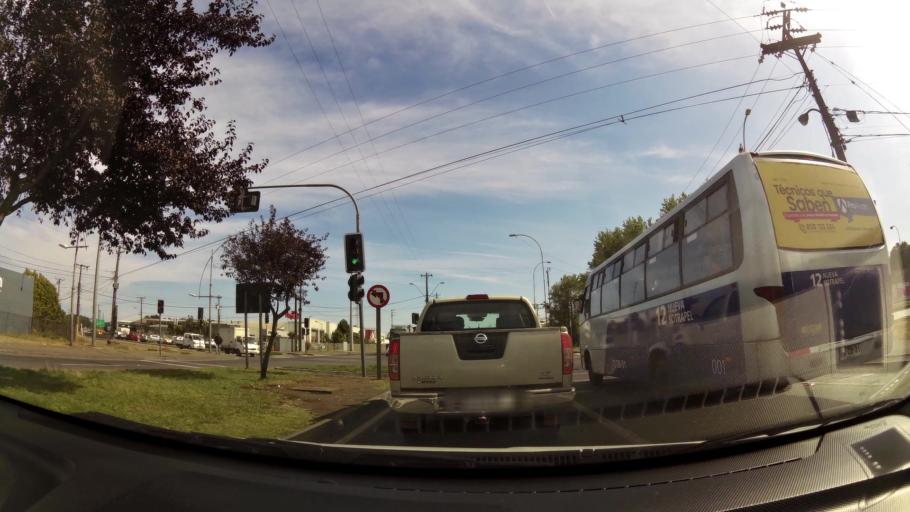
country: CL
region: Biobio
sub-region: Provincia de Concepcion
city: Talcahuano
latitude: -36.7766
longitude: -73.1130
